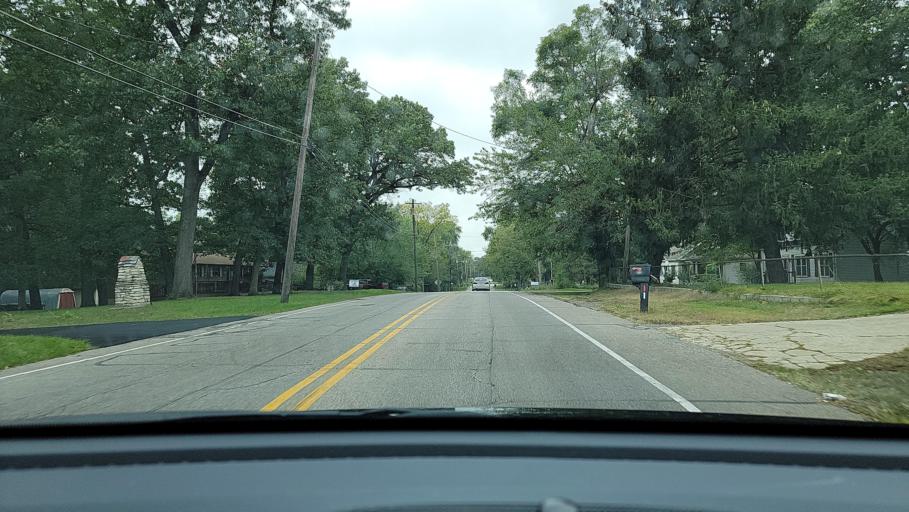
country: US
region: Indiana
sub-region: Lake County
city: Lake Station
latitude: 41.5750
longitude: -87.2128
